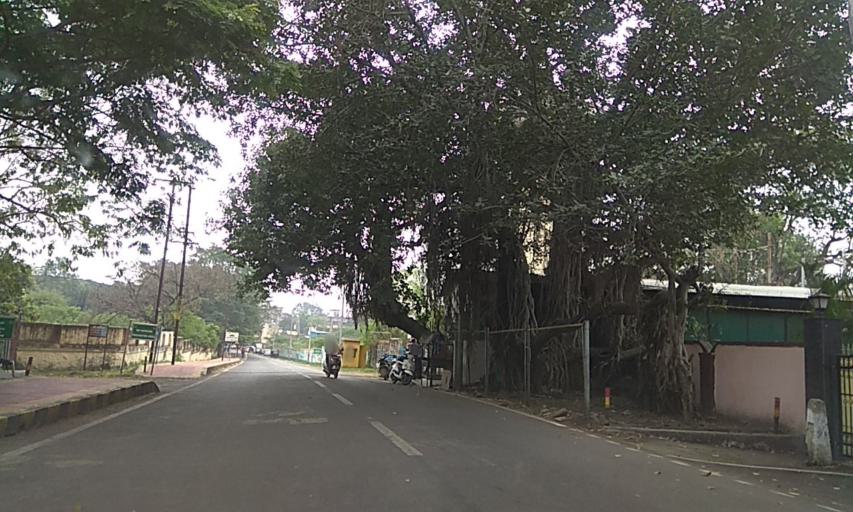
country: IN
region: Maharashtra
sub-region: Pune Division
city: Khadki
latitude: 18.5535
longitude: 73.8532
